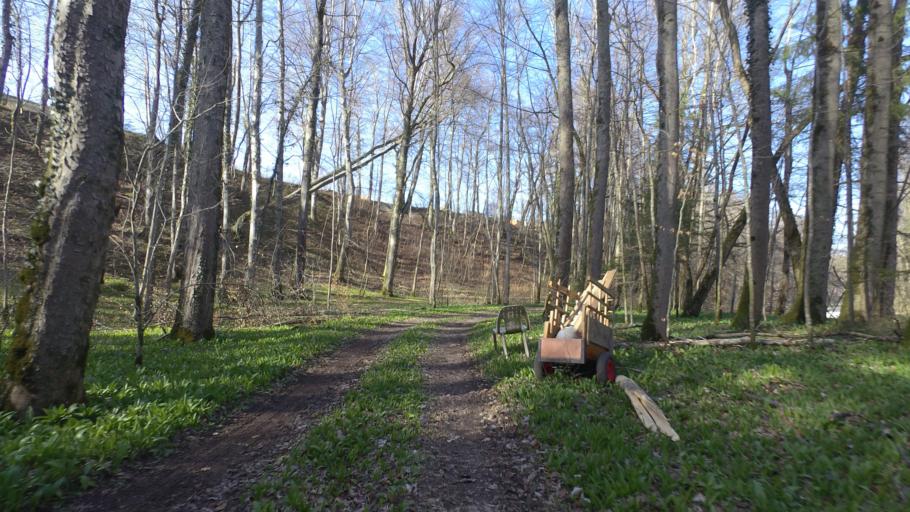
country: DE
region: Bavaria
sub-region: Upper Bavaria
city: Nussdorf
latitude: 47.9189
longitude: 12.6202
